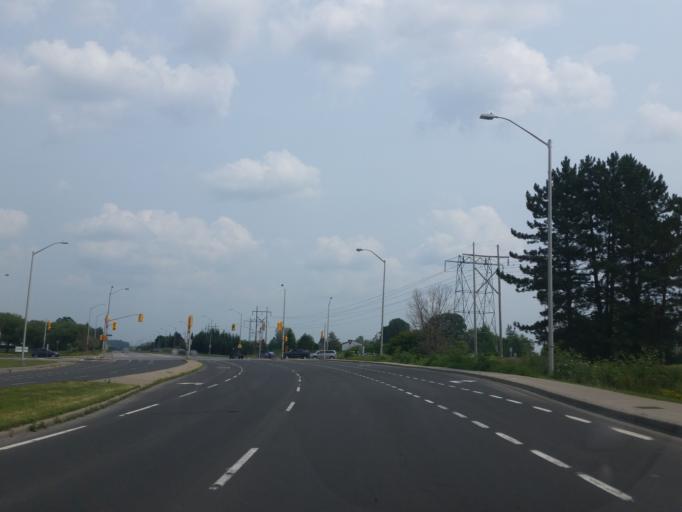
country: CA
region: Ontario
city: Bells Corners
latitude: 45.3349
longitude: -75.9069
